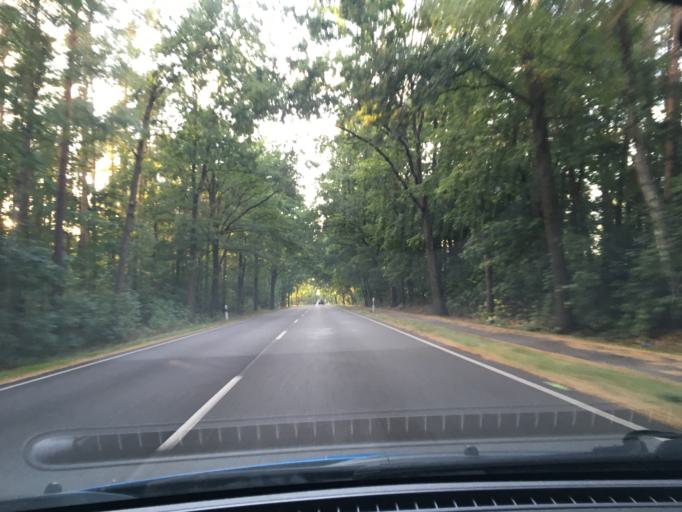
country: DE
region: Lower Saxony
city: Celle
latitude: 52.6588
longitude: 10.0536
